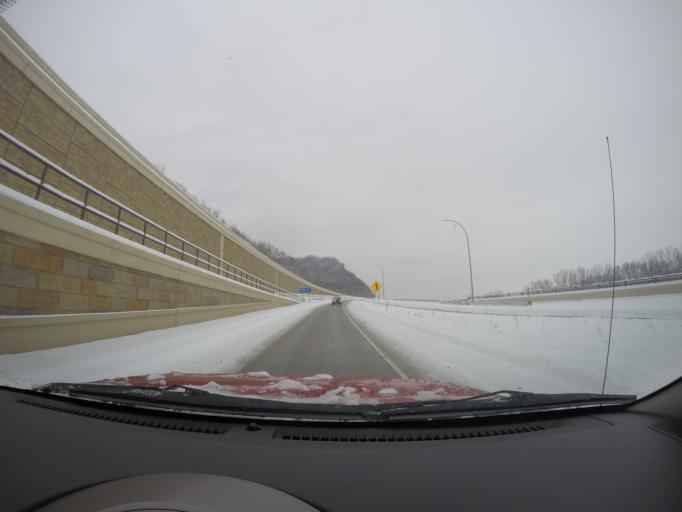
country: US
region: Minnesota
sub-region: Houston County
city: La Crescent
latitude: 43.8605
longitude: -91.3092
